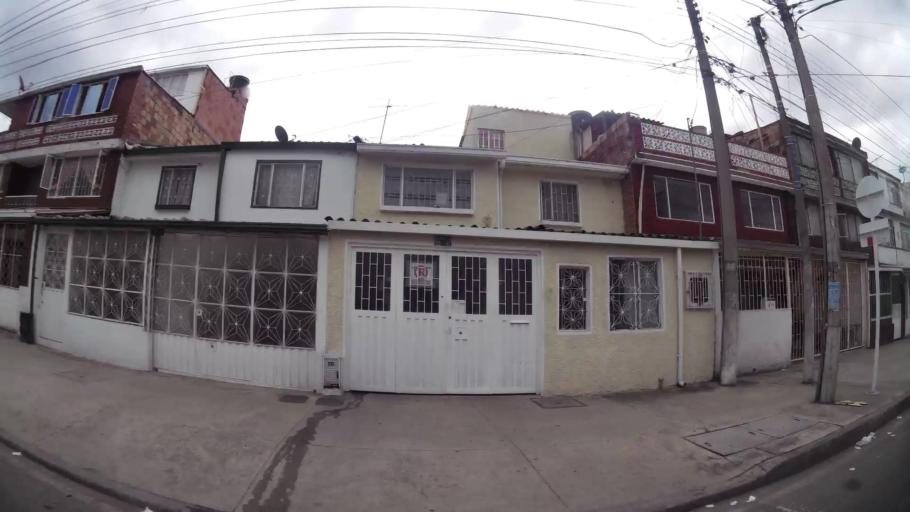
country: CO
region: Bogota D.C.
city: Barrio San Luis
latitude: 4.6966
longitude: -74.0980
